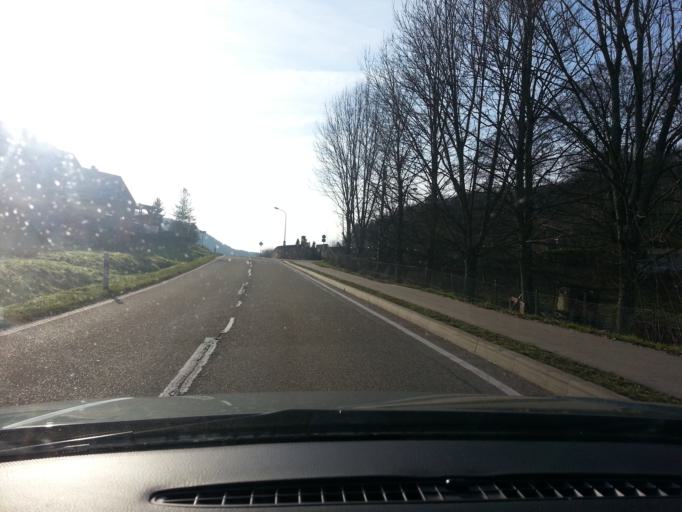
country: DE
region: Rheinland-Pfalz
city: Volkersweiler
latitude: 49.1685
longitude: 7.9346
